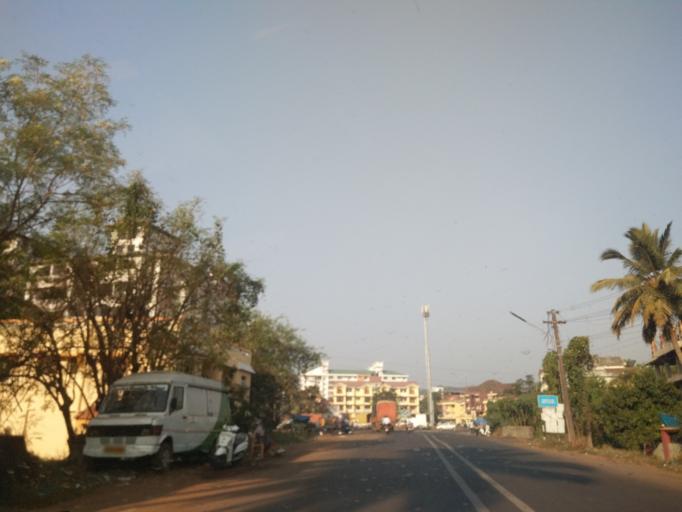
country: IN
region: Goa
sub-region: South Goa
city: Davorlim
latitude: 15.2715
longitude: 73.9798
